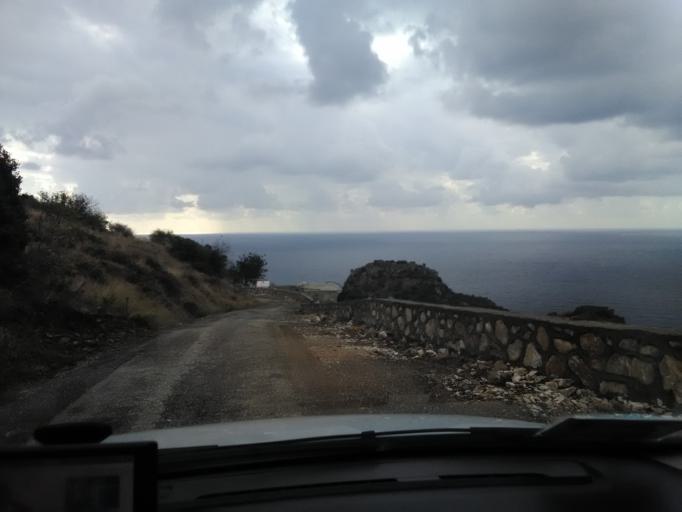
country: TR
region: Antalya
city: Gazipasa
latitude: 36.1609
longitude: 32.4219
